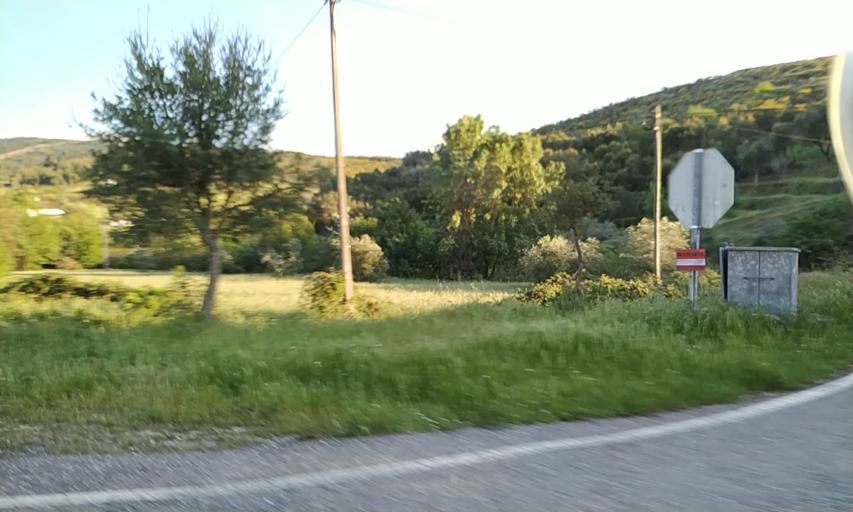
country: PT
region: Portalegre
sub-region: Portalegre
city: Sao Juliao
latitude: 39.3562
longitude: -7.3140
